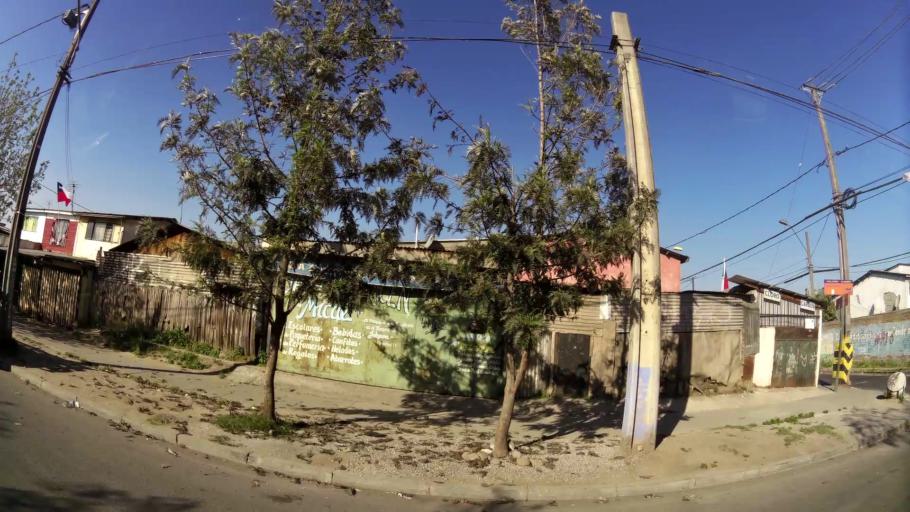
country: CL
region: Santiago Metropolitan
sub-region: Provincia de Santiago
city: La Pintana
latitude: -33.5621
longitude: -70.6126
